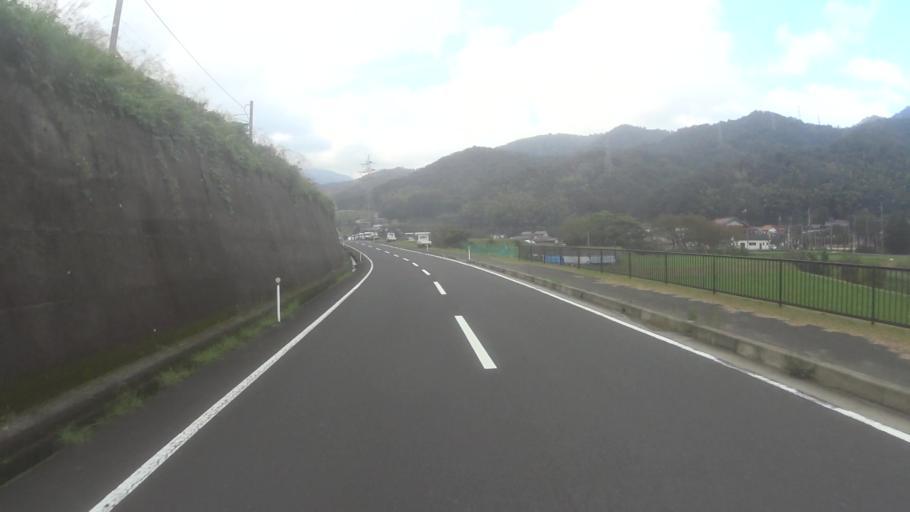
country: JP
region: Kyoto
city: Miyazu
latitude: 35.5066
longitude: 135.1829
